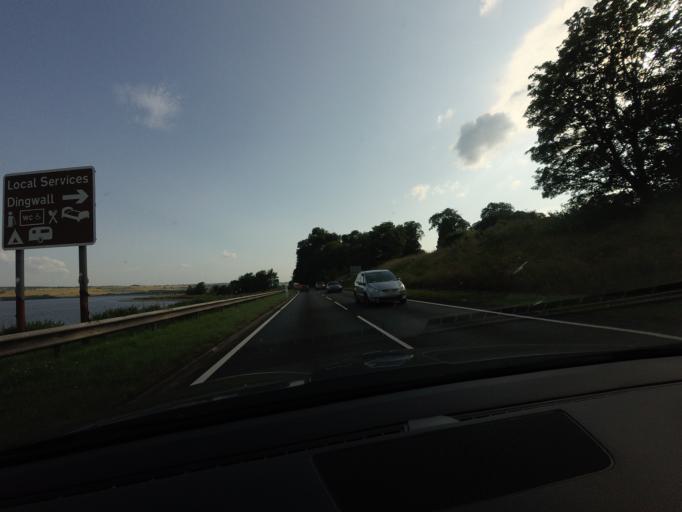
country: GB
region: Scotland
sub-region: Highland
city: Evanton
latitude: 57.6301
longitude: -4.3664
